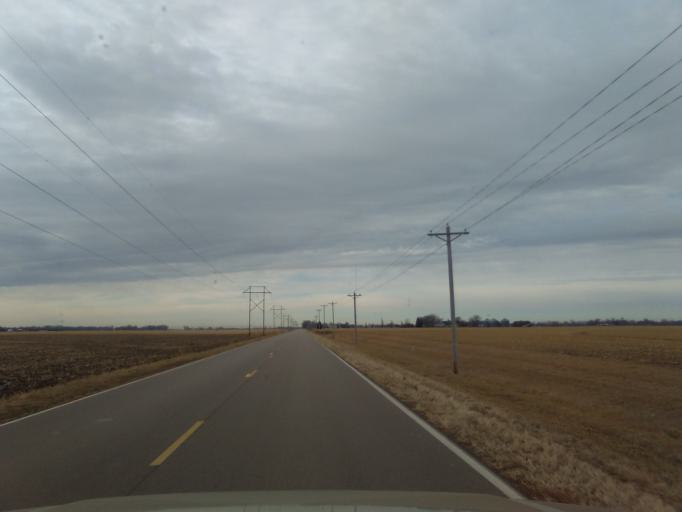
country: US
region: Nebraska
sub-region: Buffalo County
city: Gibbon
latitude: 40.6550
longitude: -98.8256
